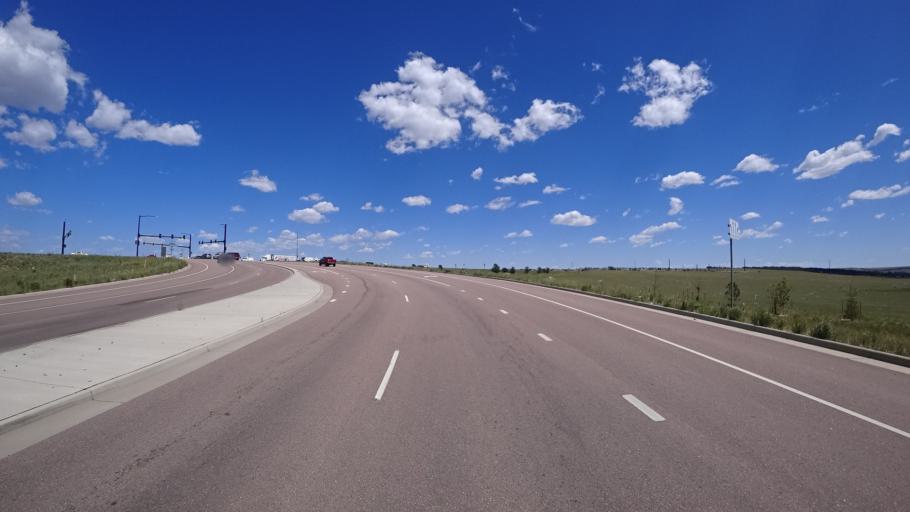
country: US
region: Colorado
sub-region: El Paso County
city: Cimarron Hills
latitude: 38.8509
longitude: -104.6812
